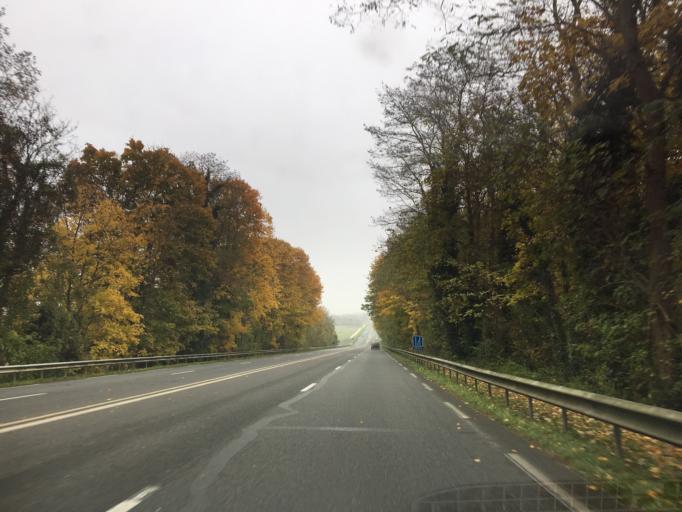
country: FR
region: Ile-de-France
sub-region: Departement de Seine-et-Marne
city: Vernou-la-Celle-sur-Seine
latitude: 48.3613
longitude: 2.8696
